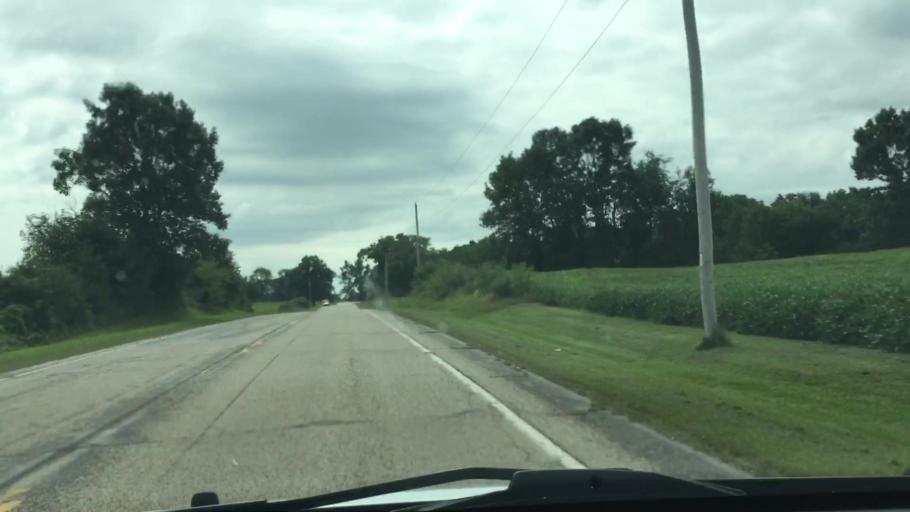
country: US
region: Wisconsin
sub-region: Dane County
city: Belleville
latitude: 42.8900
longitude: -89.4819
